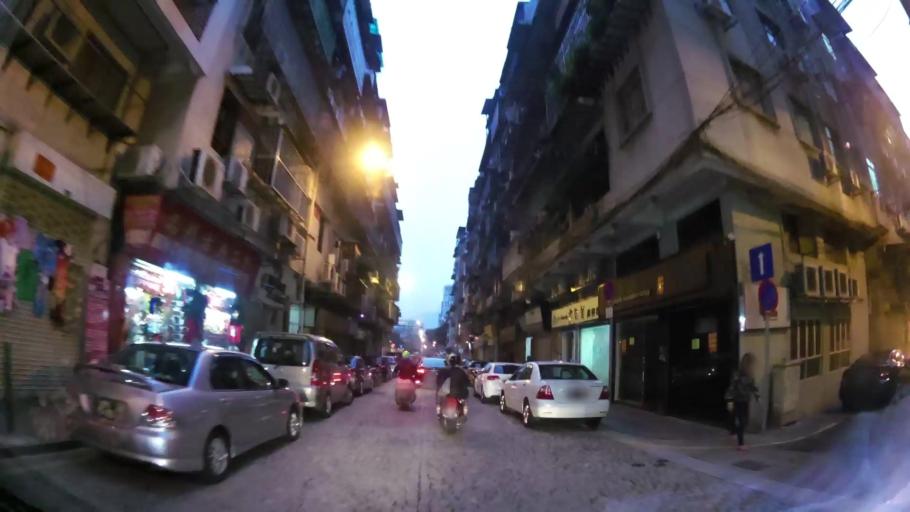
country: MO
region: Macau
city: Macau
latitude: 22.1980
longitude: 113.5428
